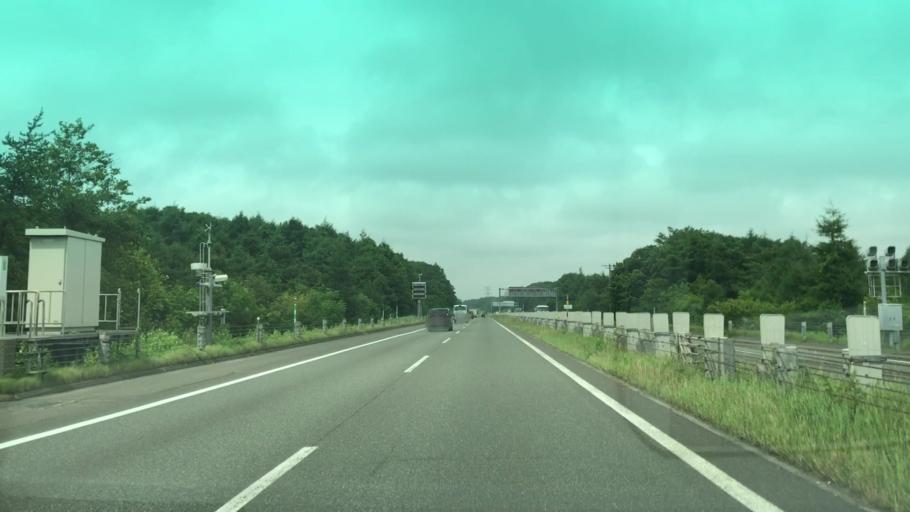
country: JP
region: Hokkaido
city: Tomakomai
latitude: 42.7184
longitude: 141.6525
